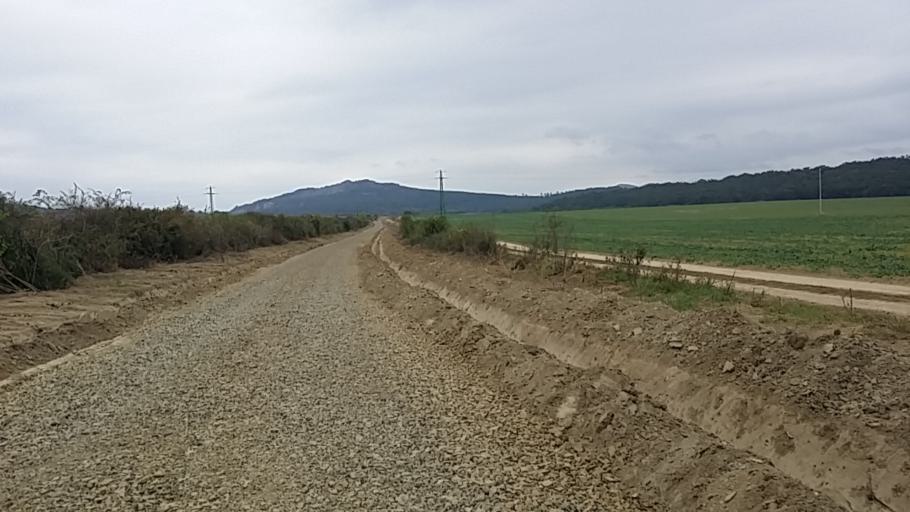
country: HU
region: Pest
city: Szob
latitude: 47.8288
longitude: 18.8723
